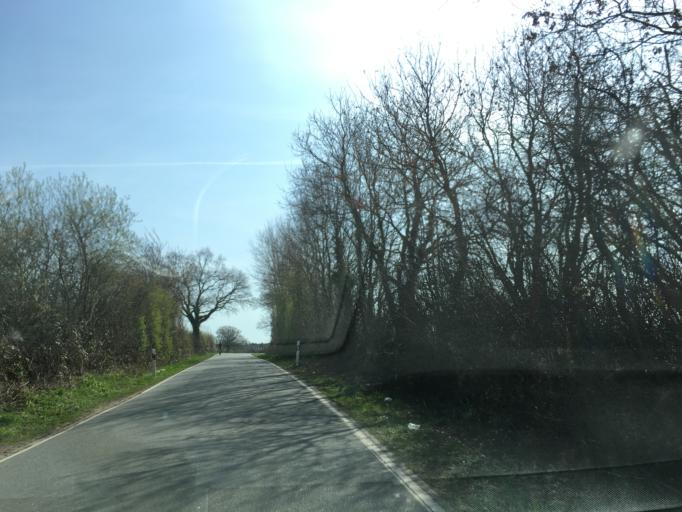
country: DE
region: Schleswig-Holstein
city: Felm
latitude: 54.4057
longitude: 10.0580
